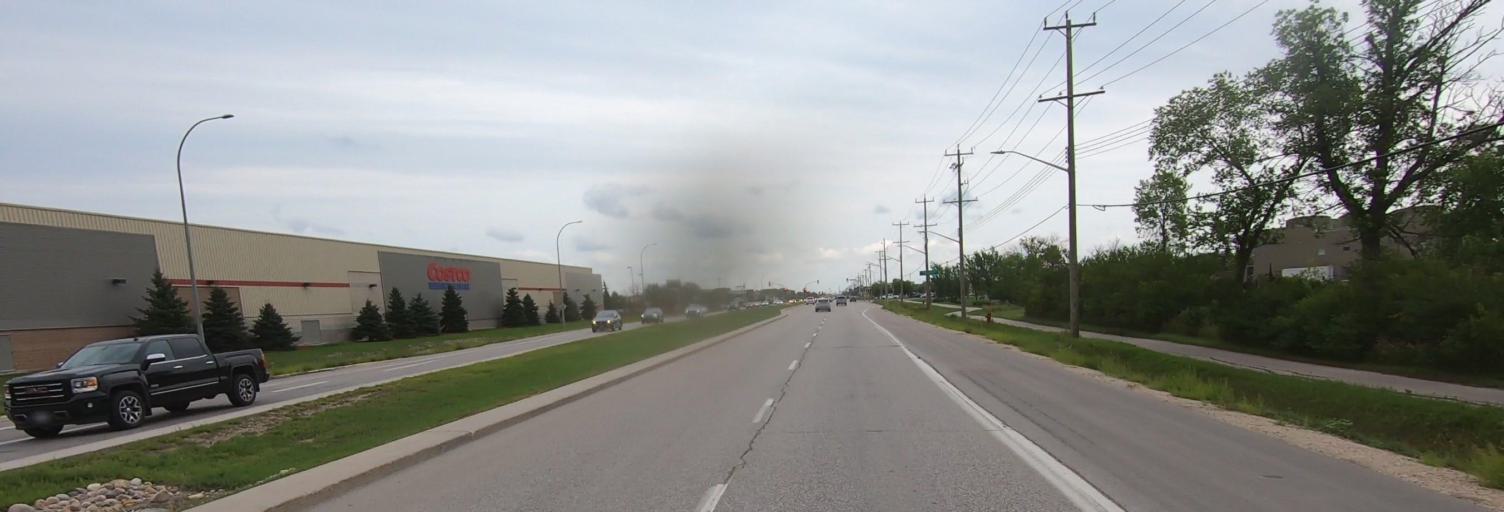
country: CA
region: Manitoba
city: Winnipeg
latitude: 49.8184
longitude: -97.2091
